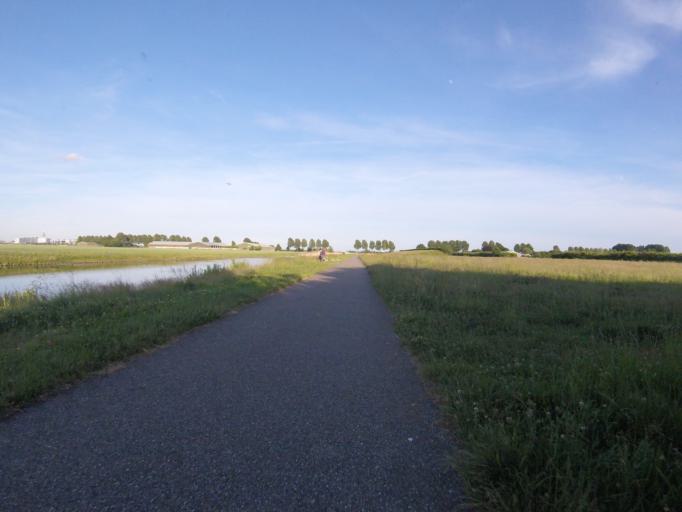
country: NL
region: North Holland
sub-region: Gemeente Haarlemmermeer
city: Hoofddorp
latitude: 52.3041
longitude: 4.7199
